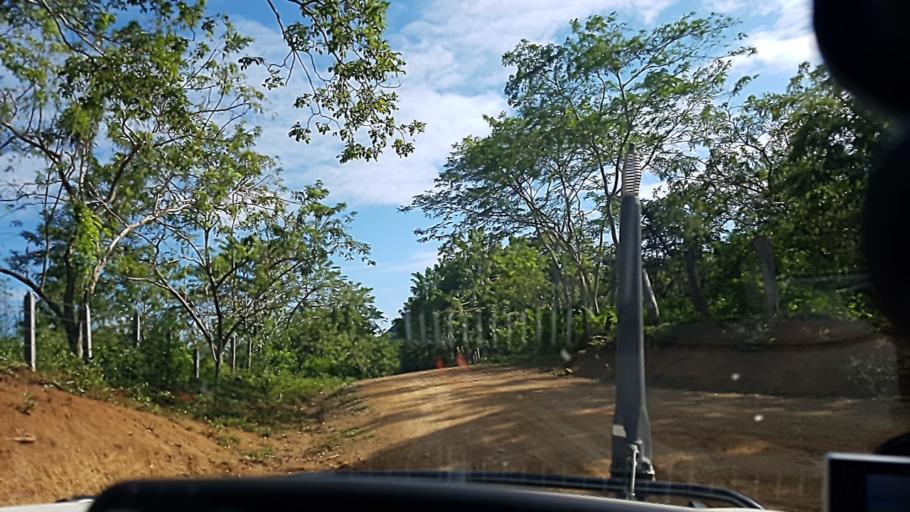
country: NI
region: Rivas
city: Tola
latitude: 11.5254
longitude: -86.1423
